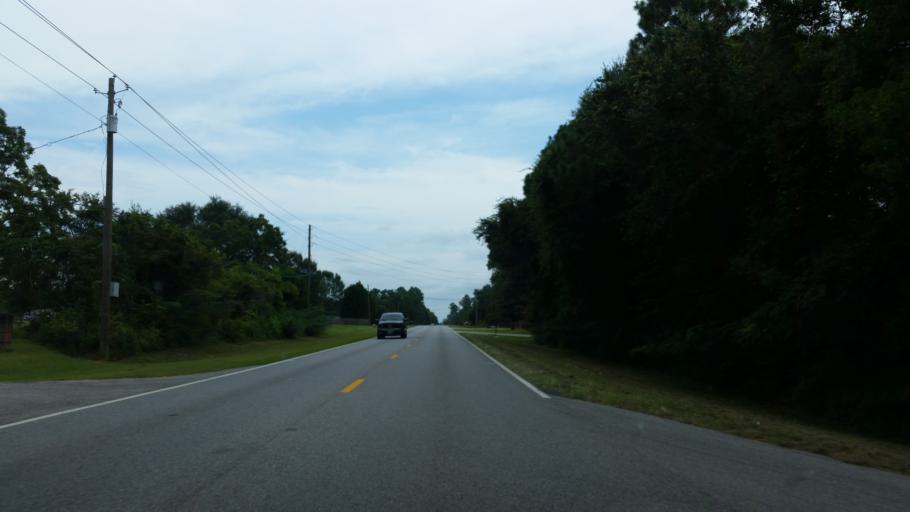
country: US
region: Florida
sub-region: Santa Rosa County
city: Wallace
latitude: 30.6534
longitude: -87.1896
